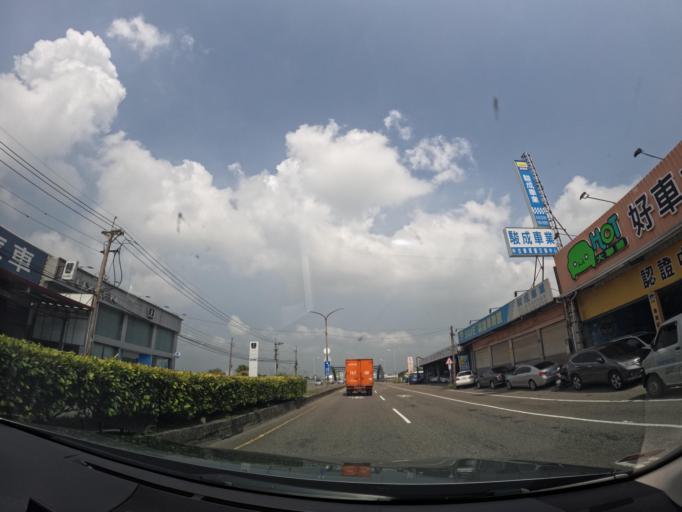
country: TW
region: Taiwan
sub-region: Yunlin
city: Douliu
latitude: 23.6984
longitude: 120.4602
